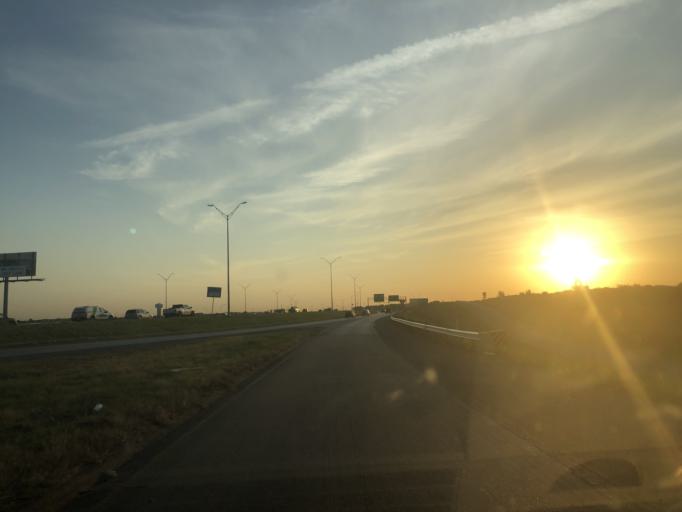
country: US
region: Texas
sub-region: Tarrant County
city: Sansom Park
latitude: 32.8044
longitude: -97.4239
